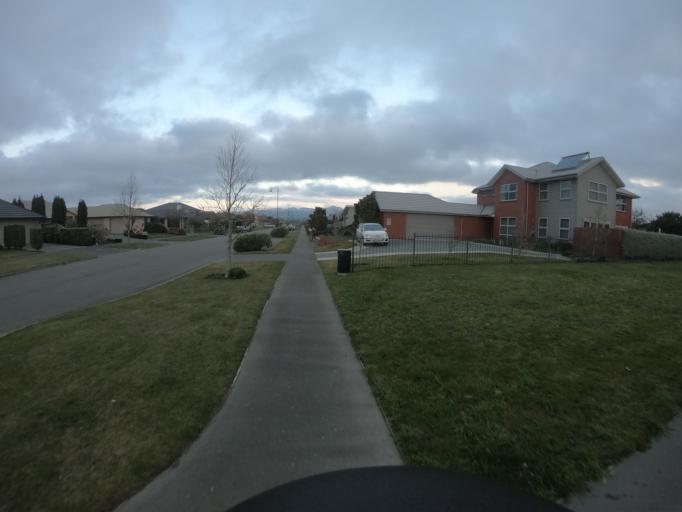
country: NZ
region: Canterbury
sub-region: Selwyn District
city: Prebbleton
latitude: -43.5652
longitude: 172.5610
